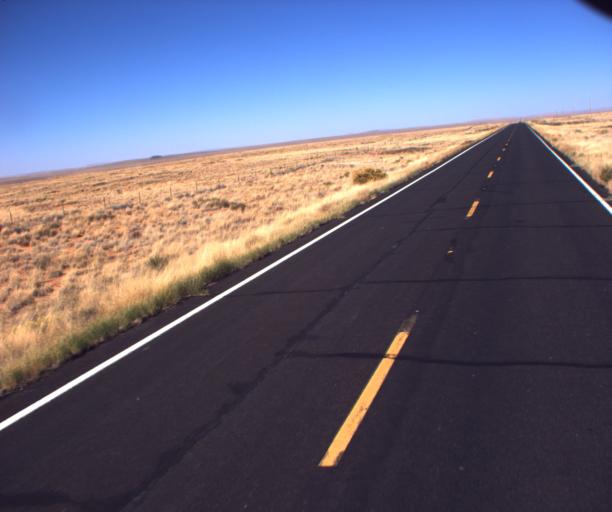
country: US
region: Arizona
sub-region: Navajo County
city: Dilkon
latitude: 35.5337
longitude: -110.4466
